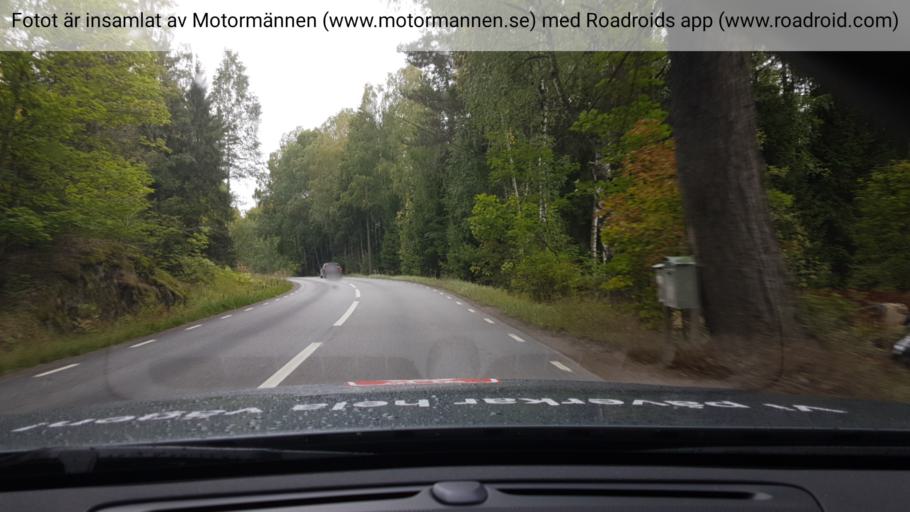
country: SE
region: Stockholm
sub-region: Botkyrka Kommun
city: Tullinge
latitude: 59.1253
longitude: 17.9076
